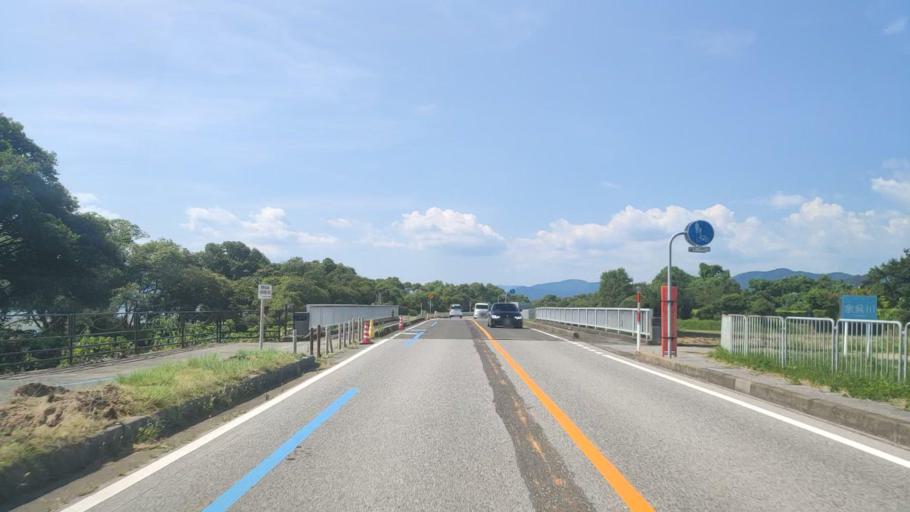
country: JP
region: Shiga Prefecture
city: Nagahama
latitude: 35.4414
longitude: 136.1900
